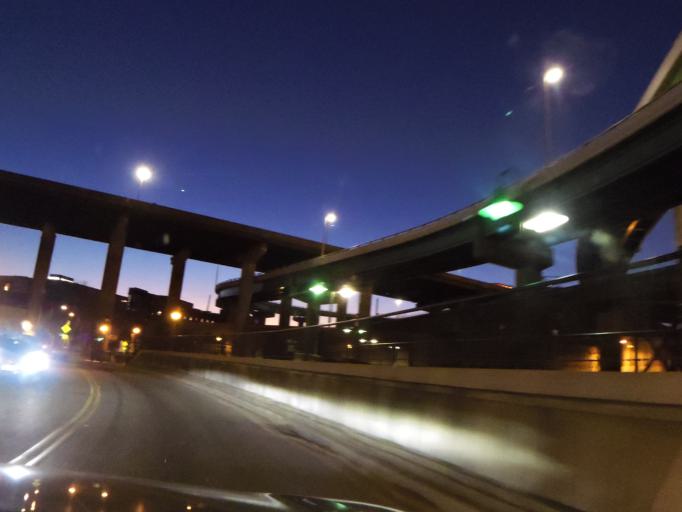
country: US
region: Virginia
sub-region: City of Richmond
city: Richmond
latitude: 37.5323
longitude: -77.4311
